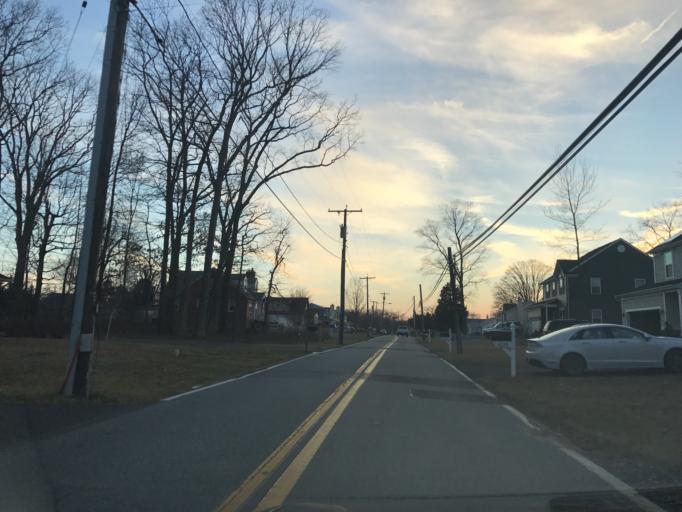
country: US
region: Maryland
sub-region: Baltimore County
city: Middle River
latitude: 39.2972
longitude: -76.4279
